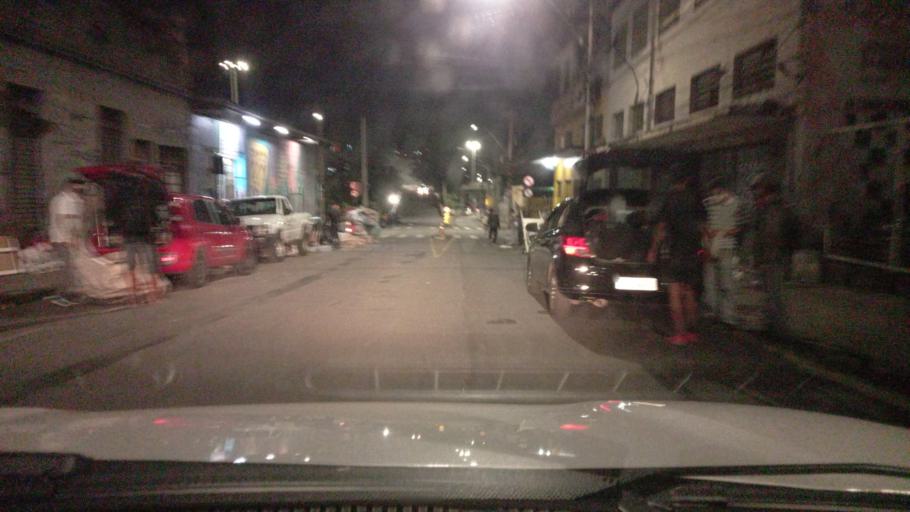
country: BR
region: Minas Gerais
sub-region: Belo Horizonte
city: Belo Horizonte
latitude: -19.9099
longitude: -43.9428
